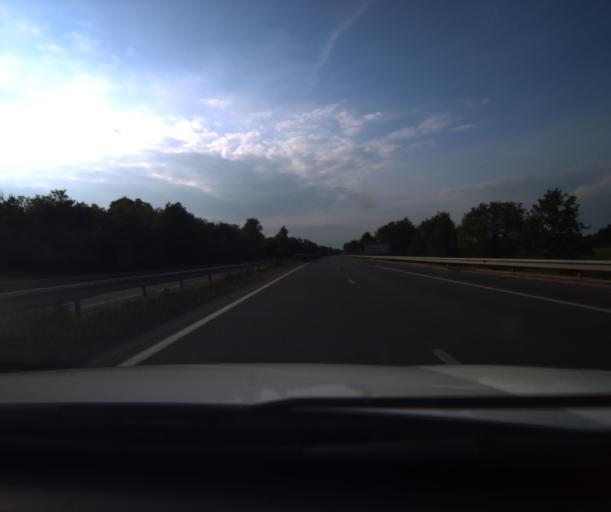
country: FR
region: Midi-Pyrenees
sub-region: Departement du Tarn-et-Garonne
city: Bressols
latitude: 43.9395
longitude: 1.2972
